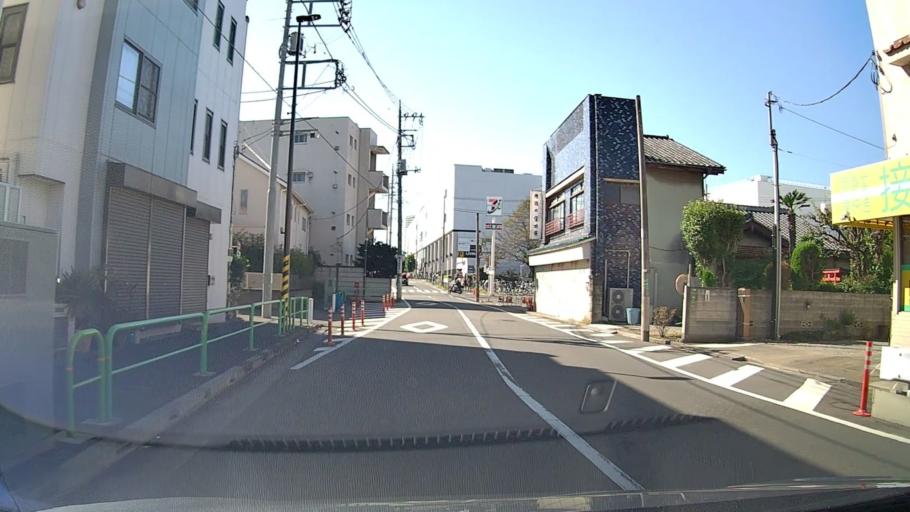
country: JP
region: Saitama
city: Wako
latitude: 35.7537
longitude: 139.5968
